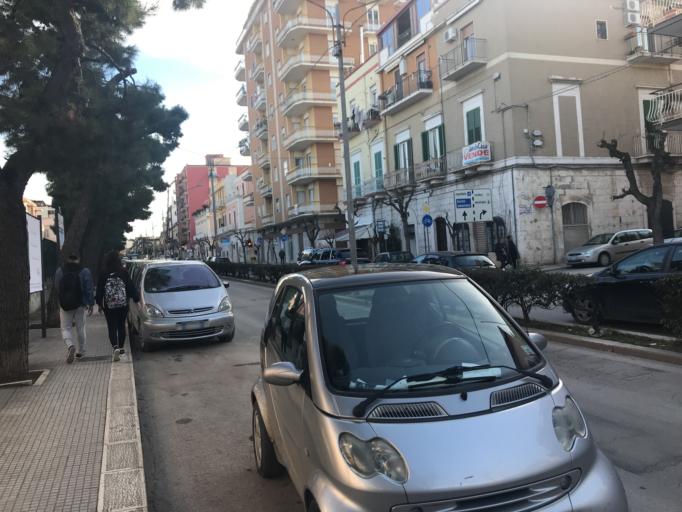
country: IT
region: Apulia
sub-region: Provincia di Bari
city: Corato
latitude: 41.1544
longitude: 16.4167
